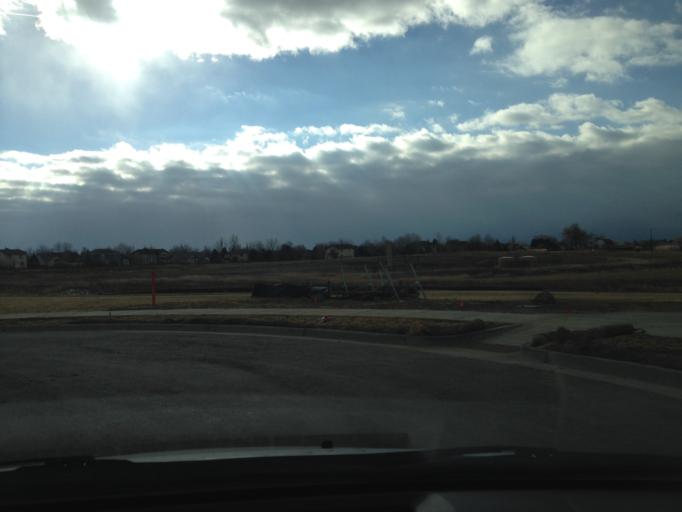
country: US
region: Colorado
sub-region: Boulder County
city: Lafayette
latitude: 40.0236
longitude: -105.0872
